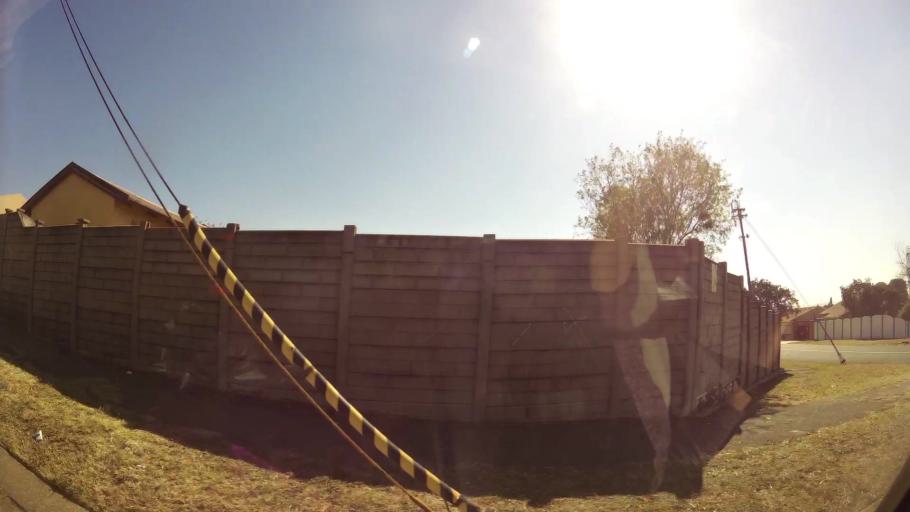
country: ZA
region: Gauteng
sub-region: City of Johannesburg Metropolitan Municipality
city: Johannesburg
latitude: -26.2554
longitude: 28.0936
